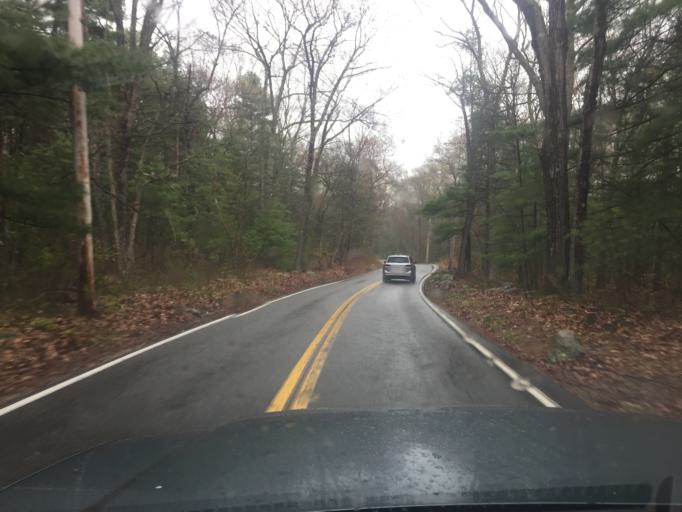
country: US
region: Massachusetts
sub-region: Norfolk County
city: Westwood
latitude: 42.2287
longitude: -71.2450
